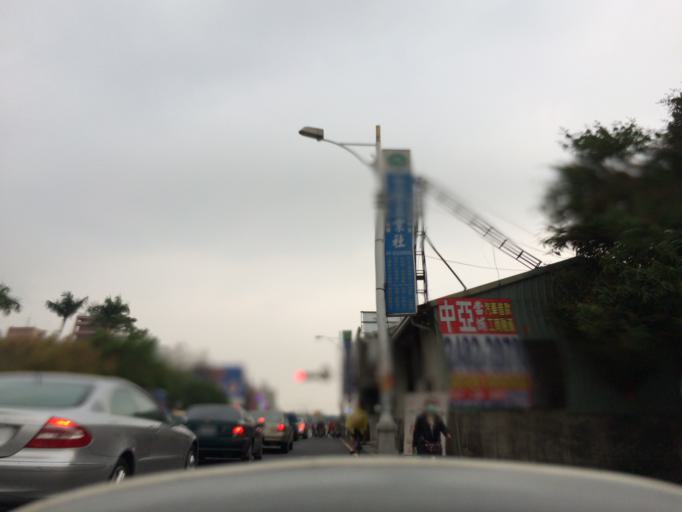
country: TW
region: Taiwan
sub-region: Taichung City
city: Taichung
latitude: 24.0554
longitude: 120.6969
